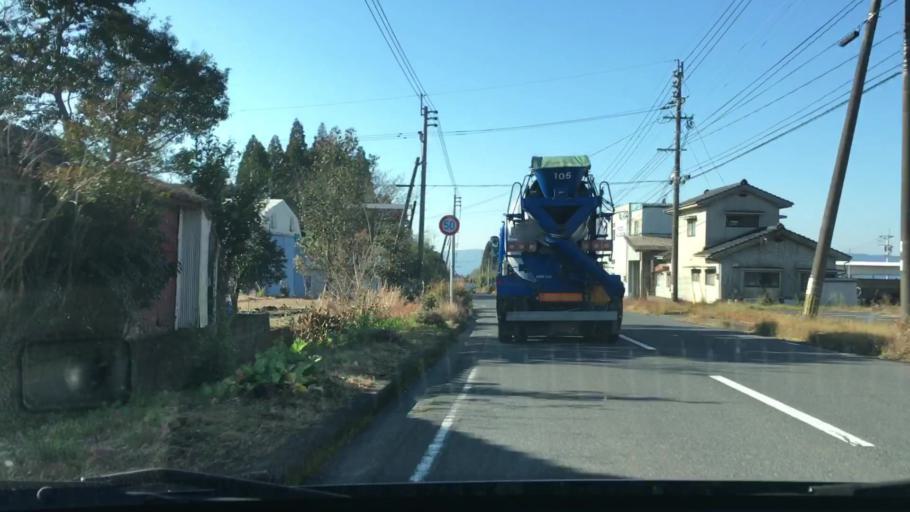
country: JP
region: Kagoshima
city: Kajiki
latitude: 31.7702
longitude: 130.6934
